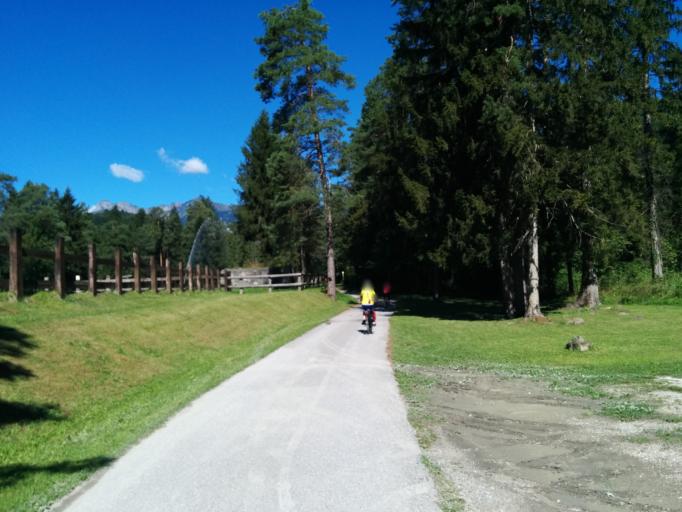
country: IT
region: Friuli Venezia Giulia
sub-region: Provincia di Udine
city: Villa Santina
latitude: 46.4085
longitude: 12.9150
